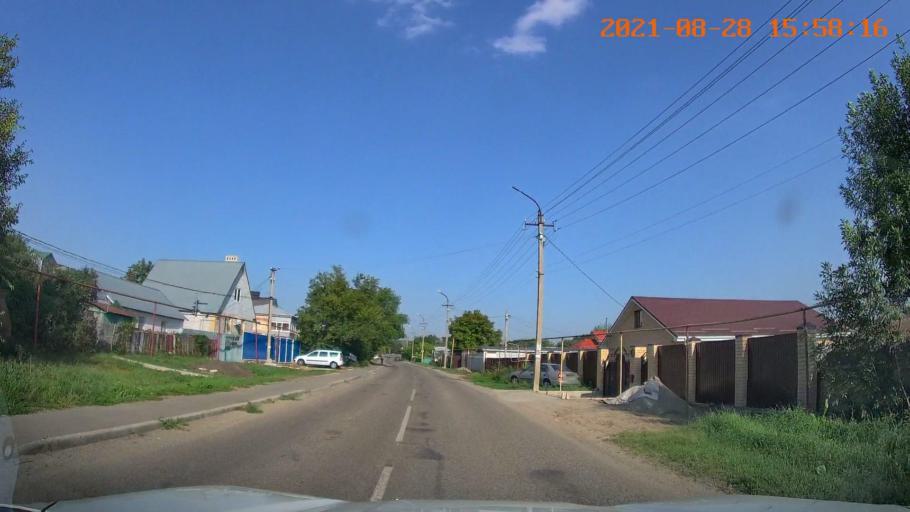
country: RU
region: Stavropol'skiy
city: Tatarka
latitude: 44.9611
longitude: 41.9495
